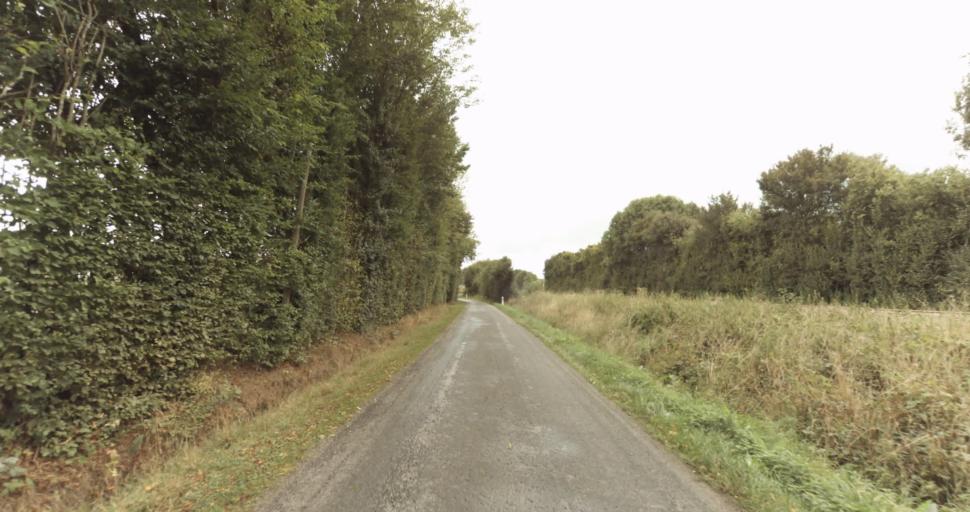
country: FR
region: Lower Normandy
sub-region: Departement de l'Orne
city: Sainte-Gauburge-Sainte-Colombe
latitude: 48.7070
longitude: 0.3524
